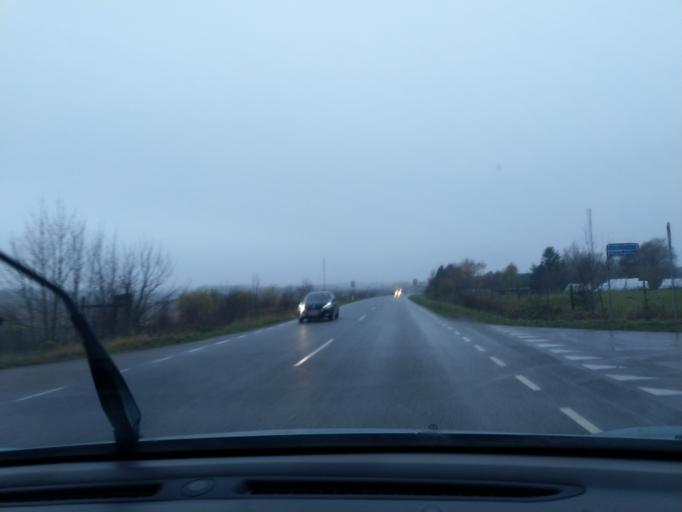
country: DK
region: Zealand
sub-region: Vordingborg Kommune
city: Orslev
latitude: 55.1287
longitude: 11.9416
